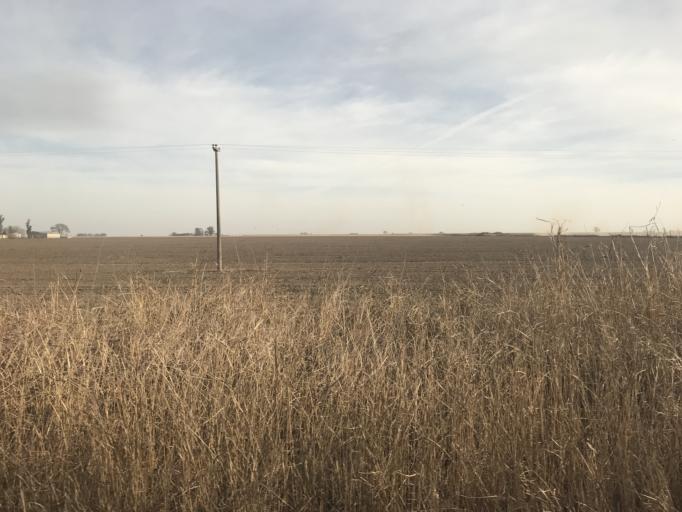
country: AR
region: Cordoba
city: Laguna Larga
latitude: -31.7482
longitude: -63.8282
